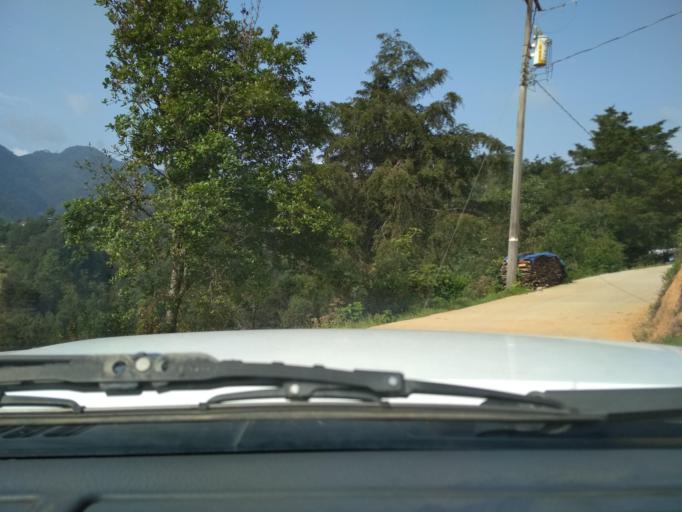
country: MX
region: Veracruz
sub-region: Soledad Atzompa
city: Tlatilpa
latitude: 18.7491
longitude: -97.1513
